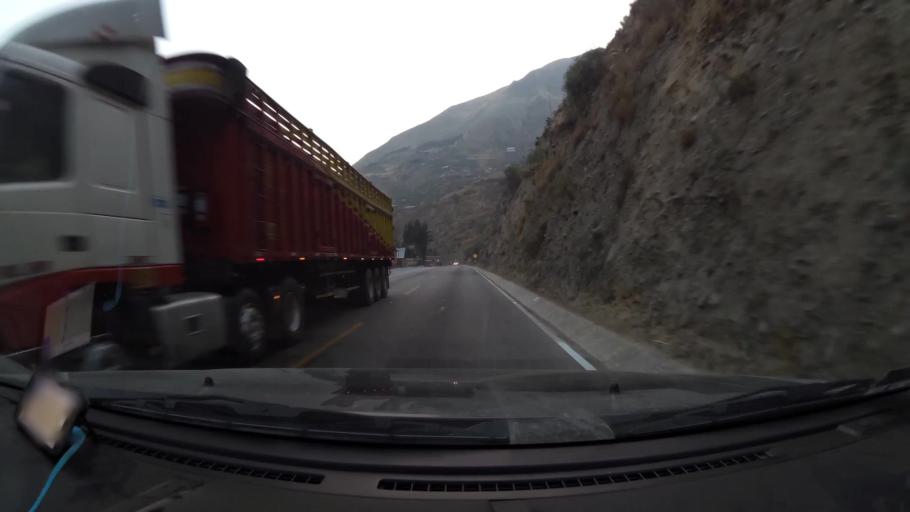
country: PE
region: Lima
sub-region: Provincia de Huarochiri
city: Matucana
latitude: -11.8598
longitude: -76.4187
